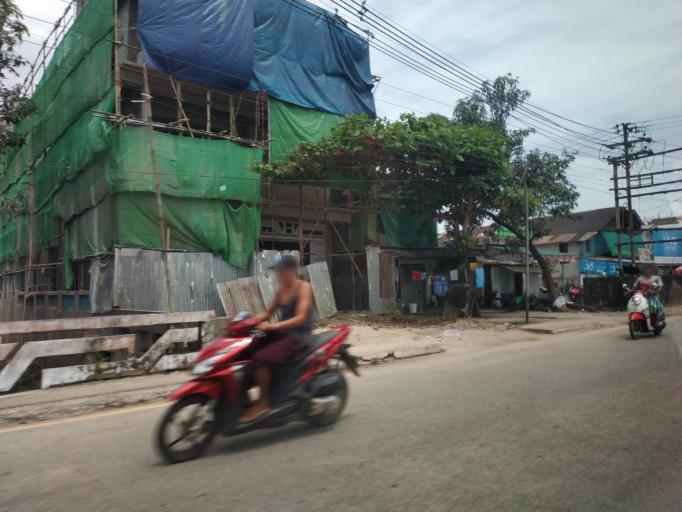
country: MM
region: Tanintharyi
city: Dawei
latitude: 14.0735
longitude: 98.2020
